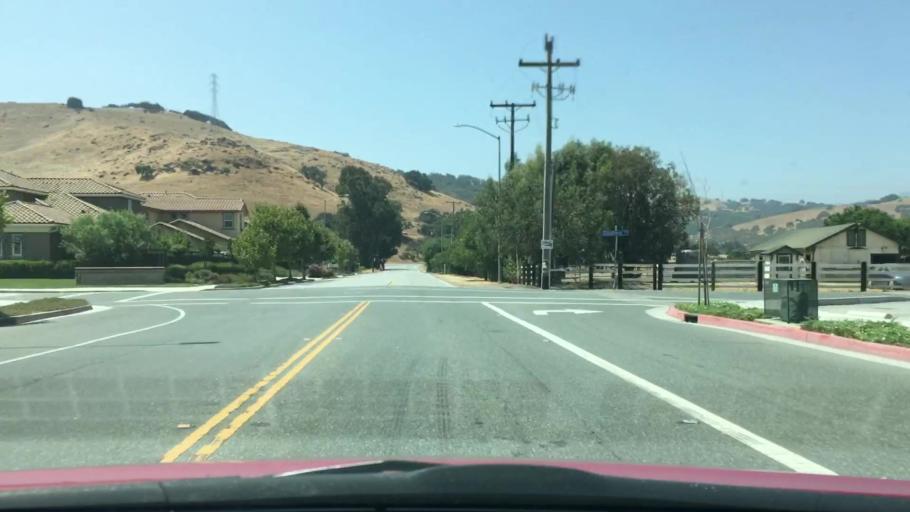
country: US
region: California
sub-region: Santa Clara County
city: Morgan Hill
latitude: 37.1532
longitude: -121.6787
